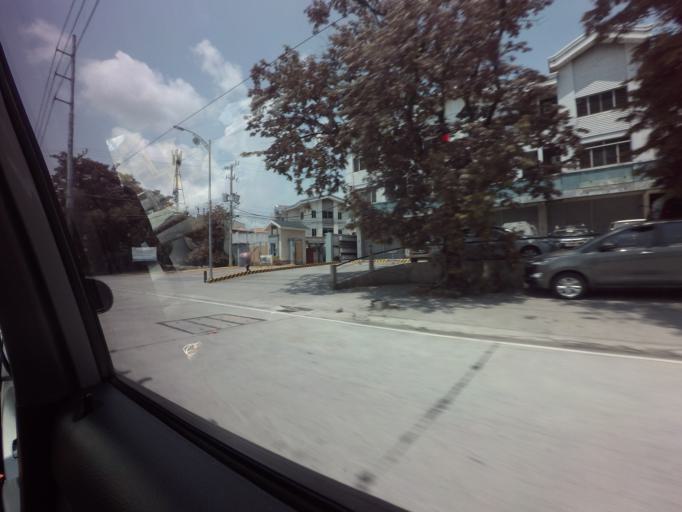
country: PH
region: Metro Manila
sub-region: City of Manila
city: Quiapo
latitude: 14.5884
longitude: 120.9966
